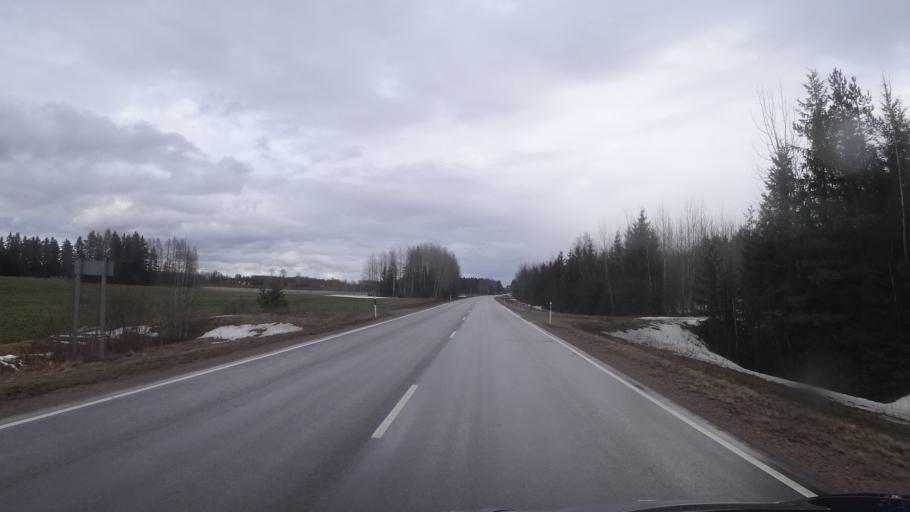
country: FI
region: Kymenlaakso
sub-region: Kouvola
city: Elimaeki
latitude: 60.6908
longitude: 26.5635
